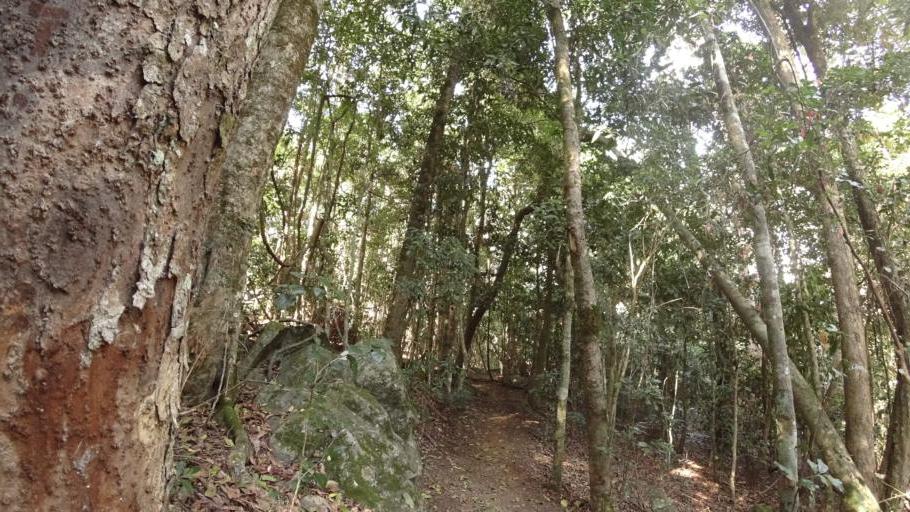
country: AU
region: Queensland
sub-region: Moreton Bay
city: Highvale
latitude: -27.3998
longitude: 152.7911
